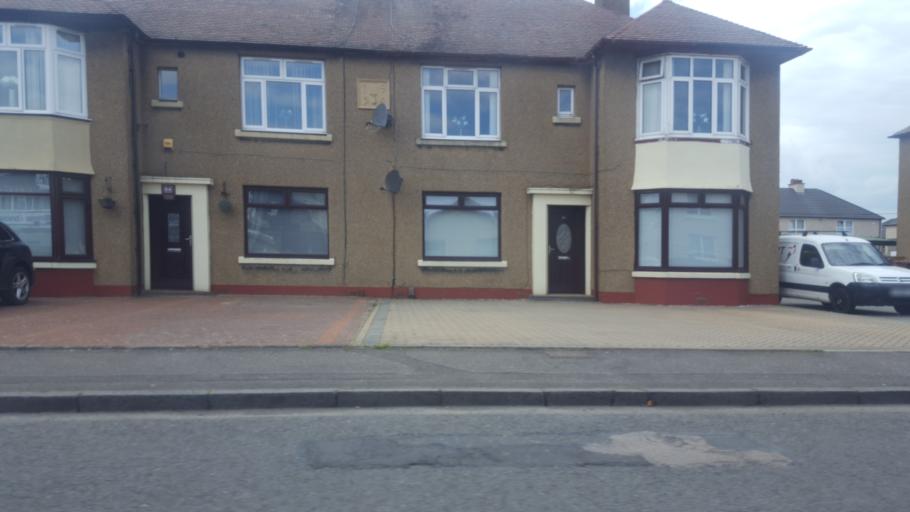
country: GB
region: Scotland
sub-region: Falkirk
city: Grangemouth
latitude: 56.0108
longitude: -3.7240
